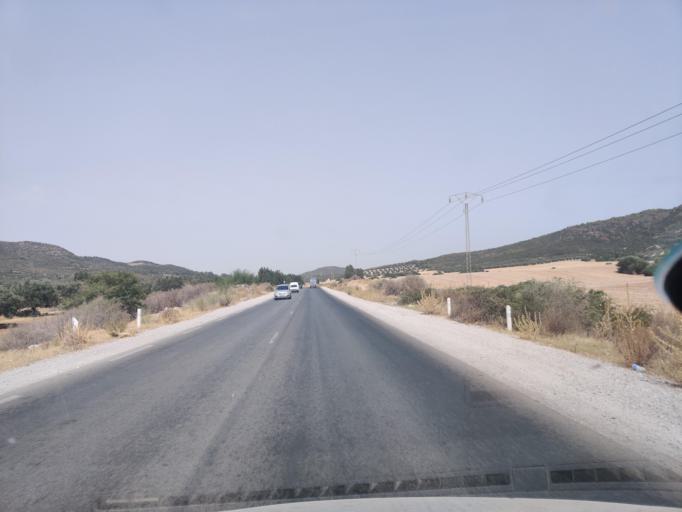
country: TN
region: Tunis
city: Hammam-Lif
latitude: 36.6292
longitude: 10.3950
